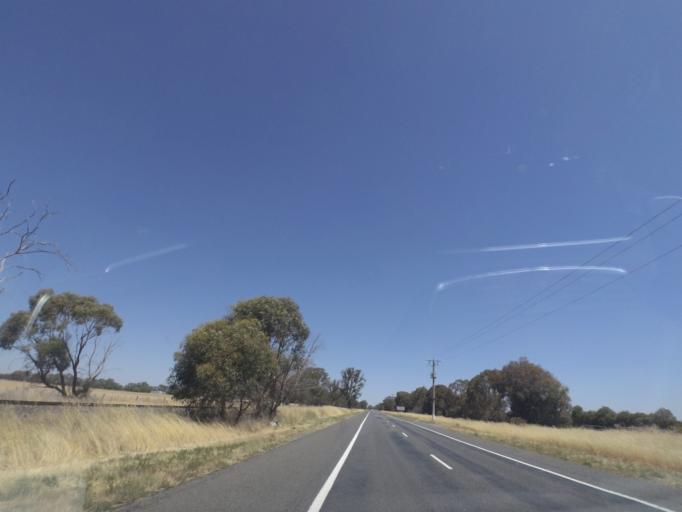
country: AU
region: Victoria
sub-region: Greater Shepparton
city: Shepparton
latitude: -36.2130
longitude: 145.4319
